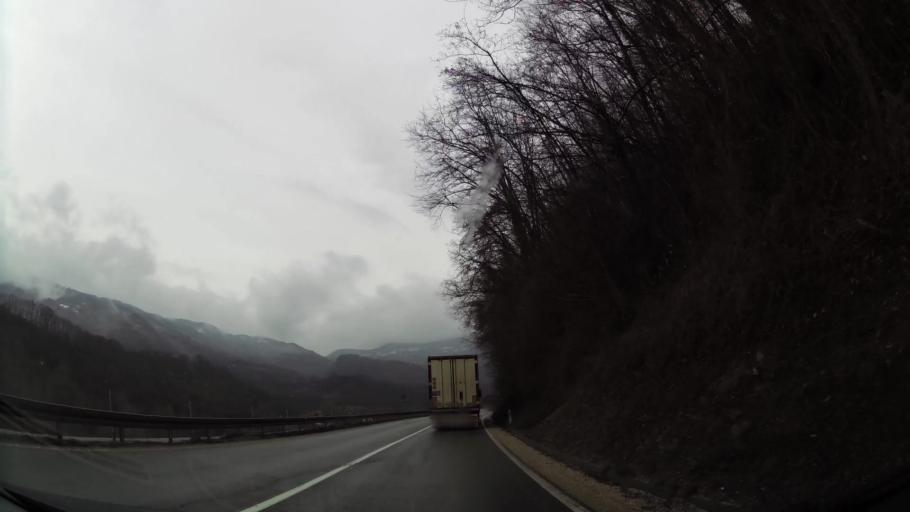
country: RS
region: Central Serbia
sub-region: Pcinjski Okrug
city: Vladicin Han
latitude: 42.7887
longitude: 22.0920
